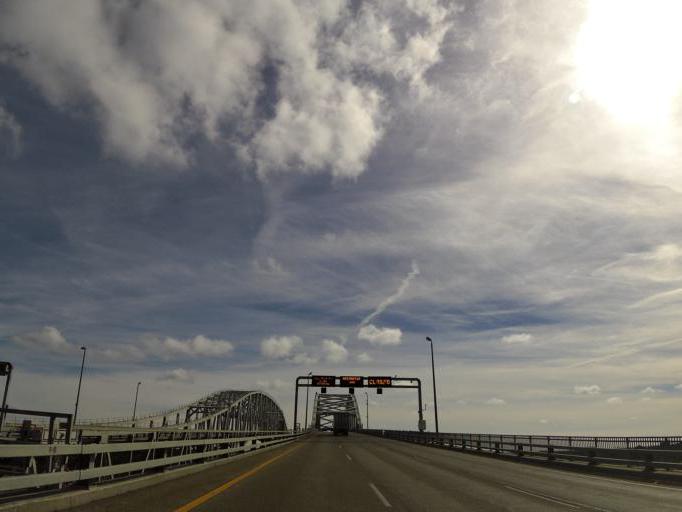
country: US
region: Michigan
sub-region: Saint Clair County
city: Port Huron
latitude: 42.9993
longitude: -82.4271
